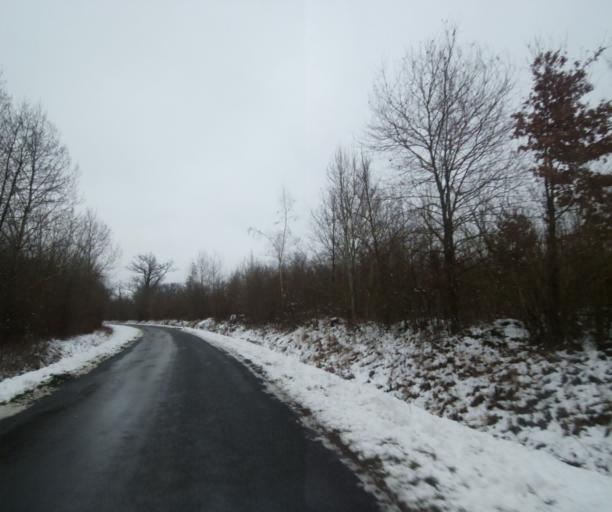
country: FR
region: Champagne-Ardenne
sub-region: Departement de la Haute-Marne
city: Laneuville-a-Remy
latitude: 48.4863
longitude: 4.8663
